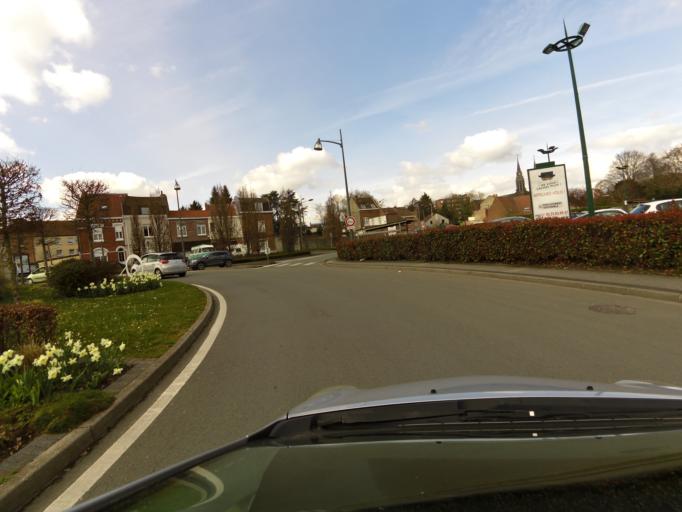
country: FR
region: Nord-Pas-de-Calais
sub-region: Departement du Nord
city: Armentieres
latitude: 50.6823
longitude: 2.8729
